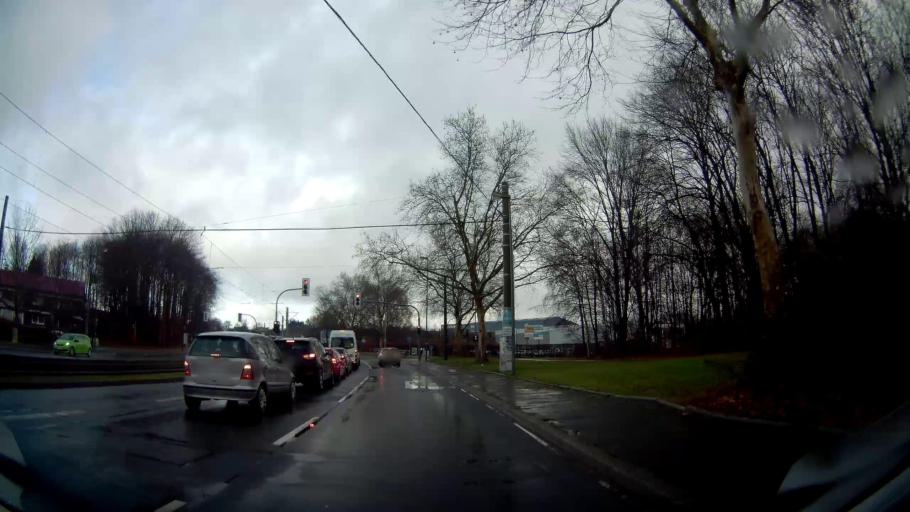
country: DE
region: North Rhine-Westphalia
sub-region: Regierungsbezirk Arnsberg
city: Herne
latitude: 51.5095
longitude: 7.2663
